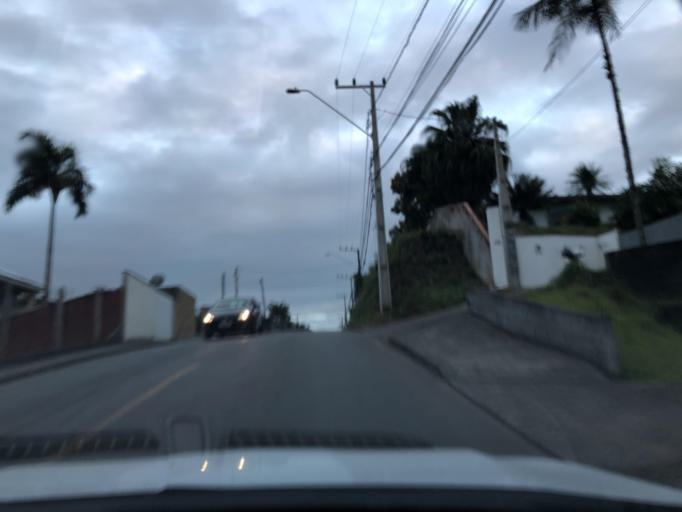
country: BR
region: Santa Catarina
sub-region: Joinville
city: Joinville
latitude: -26.2909
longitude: -48.8778
